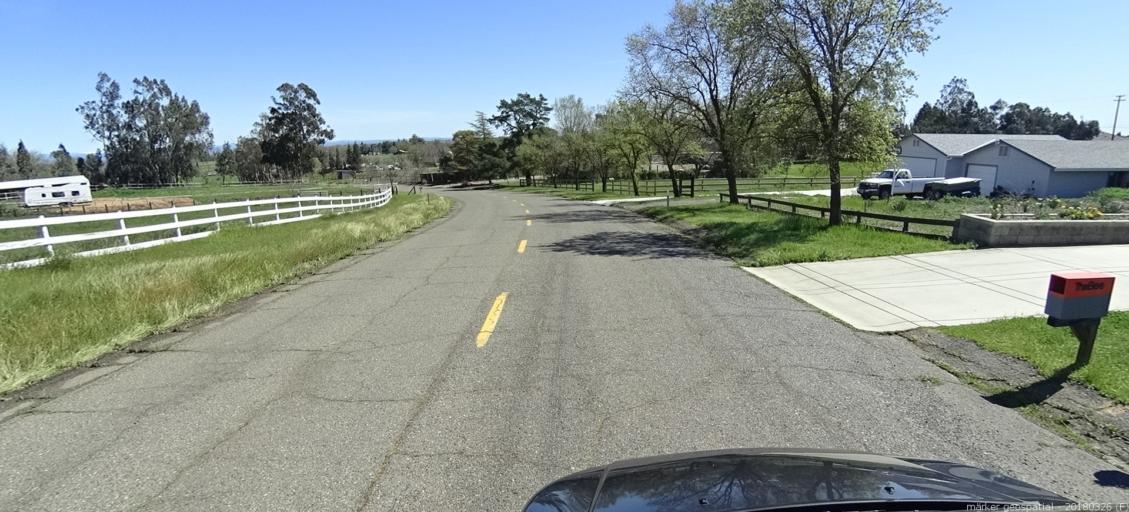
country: US
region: California
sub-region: Sacramento County
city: Wilton
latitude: 38.4773
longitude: -121.2309
